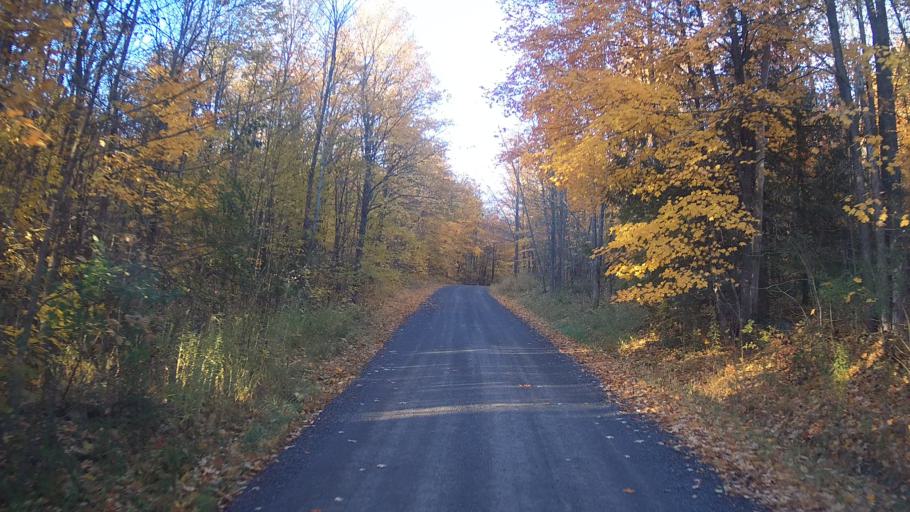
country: CA
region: Ontario
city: Arnprior
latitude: 45.3370
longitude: -76.3533
